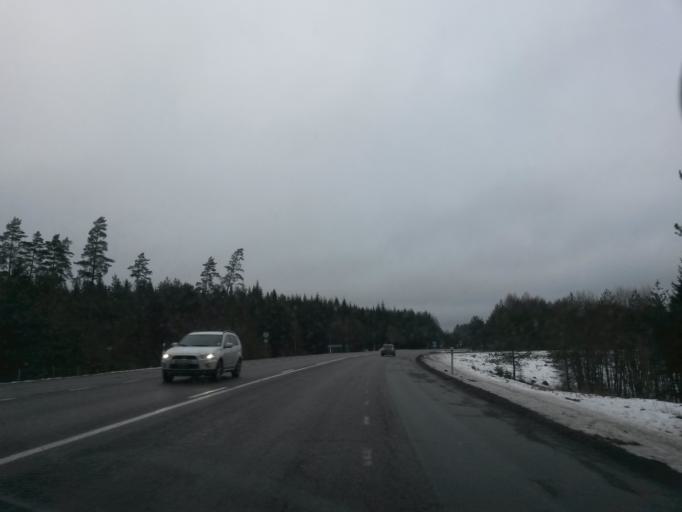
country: SE
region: Vaestra Goetaland
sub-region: Boras Kommun
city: Viskafors
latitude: 57.6106
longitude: 12.8721
